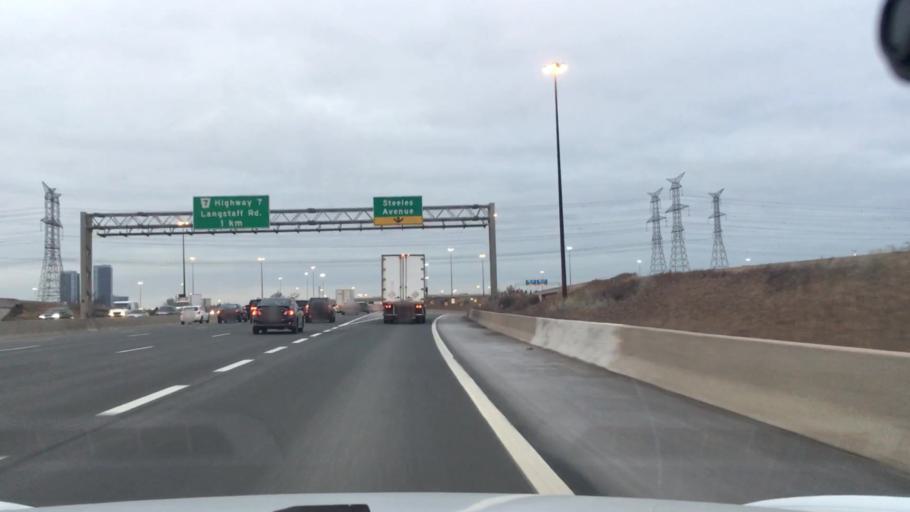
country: CA
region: Ontario
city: Concord
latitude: 43.7743
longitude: -79.5351
